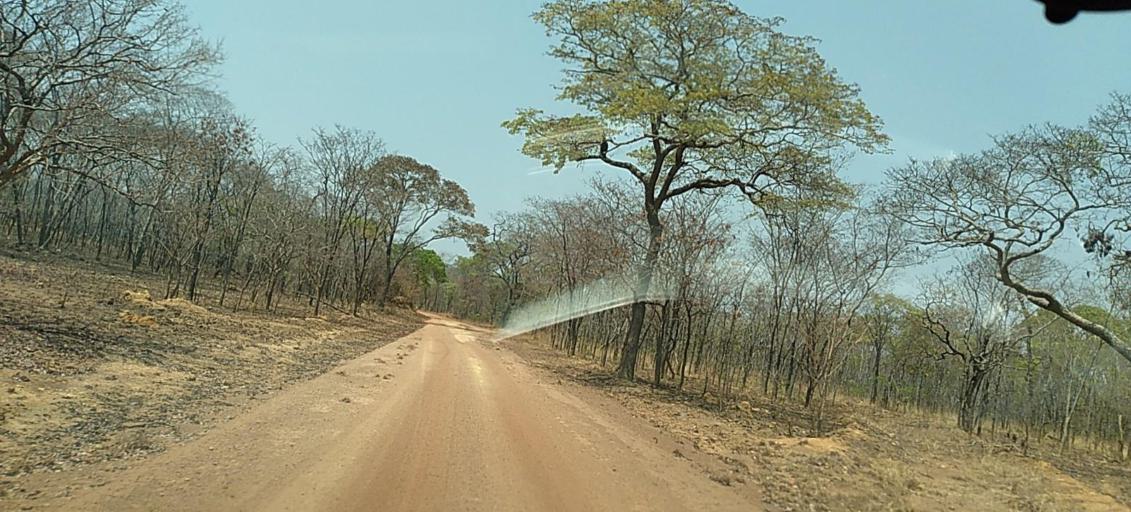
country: ZM
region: Central
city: Mumbwa
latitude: -14.2749
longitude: 26.5225
